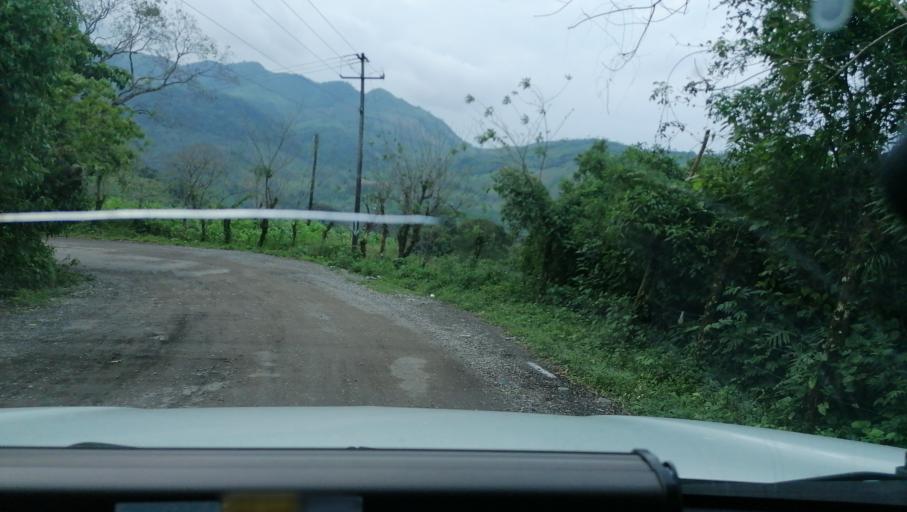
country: MX
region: Chiapas
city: Ixtacomitan
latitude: 17.3485
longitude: -93.1314
